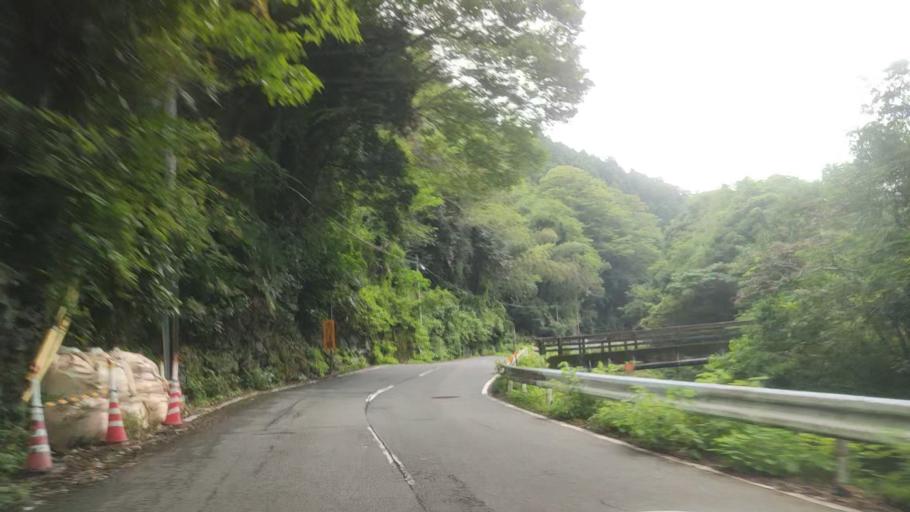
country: JP
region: Wakayama
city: Hashimoto
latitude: 34.2744
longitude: 135.5695
